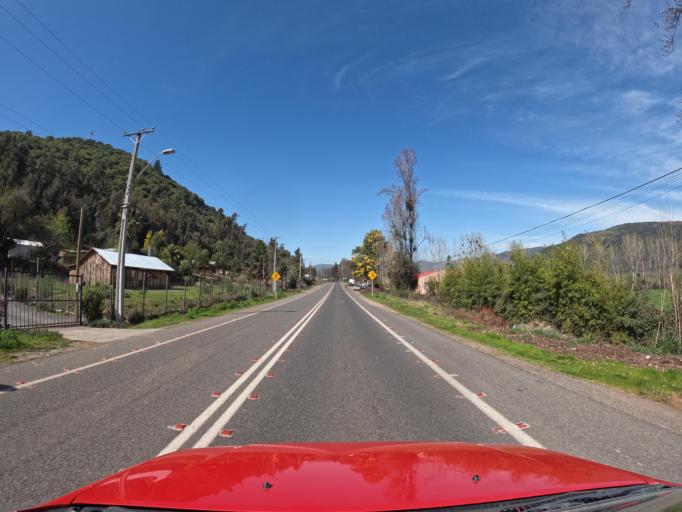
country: CL
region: Maule
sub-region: Provincia de Curico
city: Teno
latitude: -34.9785
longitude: -70.9844
